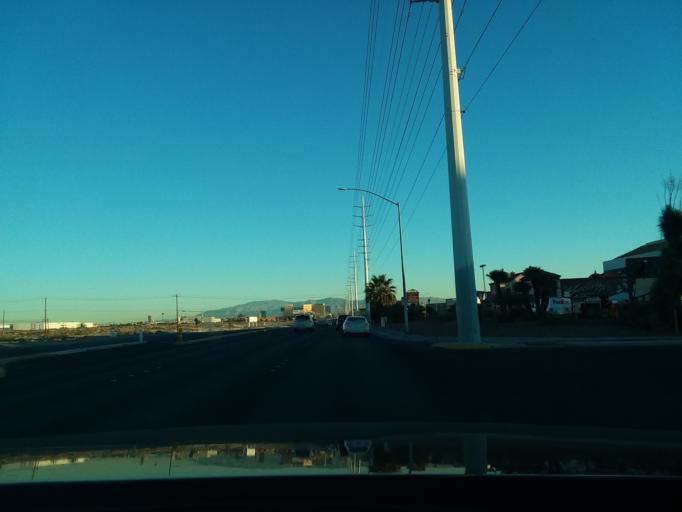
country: US
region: Nevada
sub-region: Clark County
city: Paradise
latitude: 36.0477
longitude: -115.1722
